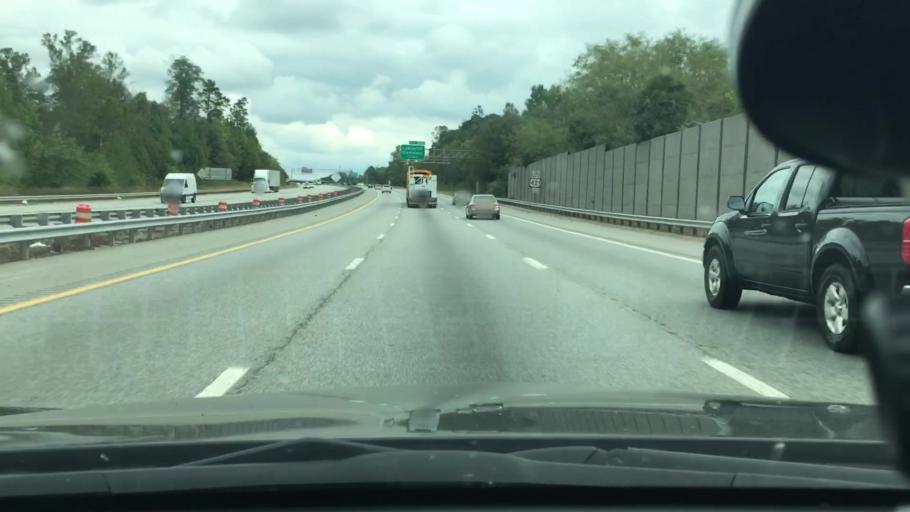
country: US
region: North Carolina
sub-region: Forsyth County
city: Clemmons
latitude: 36.0289
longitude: -80.3927
